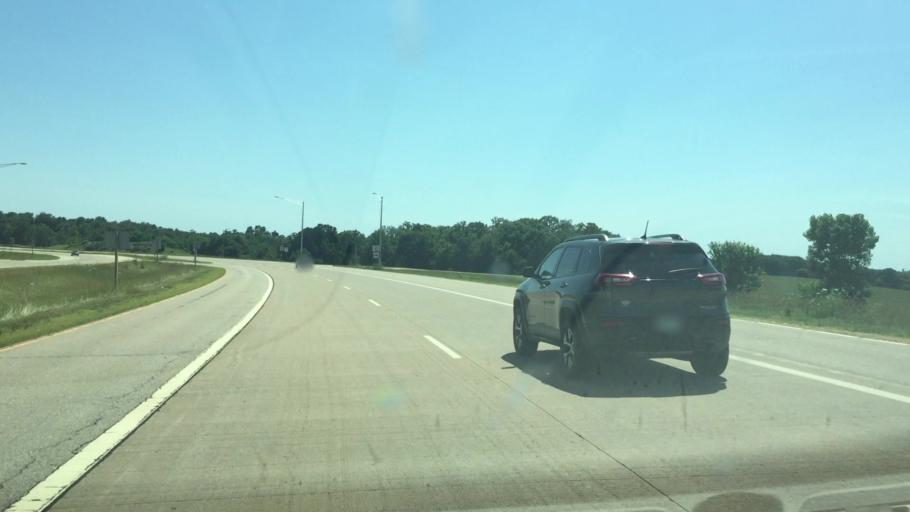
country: US
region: Wisconsin
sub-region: Grant County
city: Platteville
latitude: 42.7030
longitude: -90.5268
